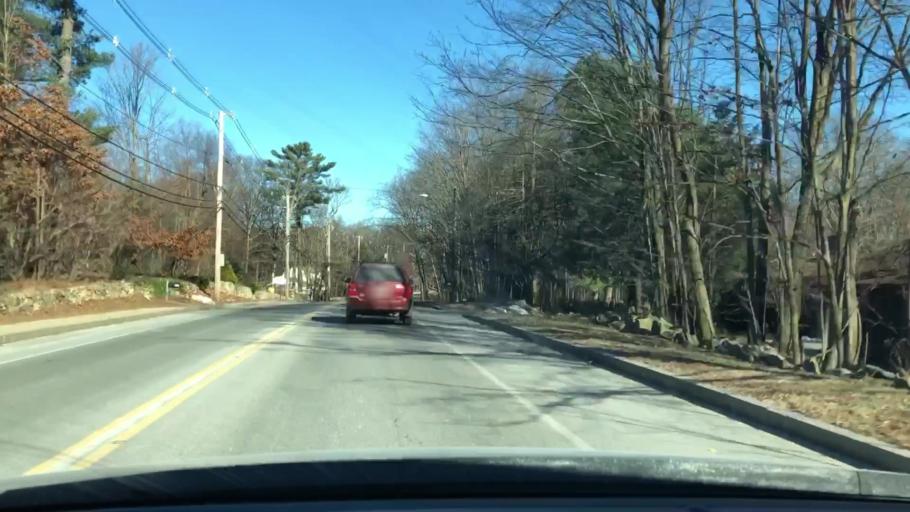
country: US
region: Massachusetts
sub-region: Norfolk County
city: Westwood
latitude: 42.2395
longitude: -71.2146
